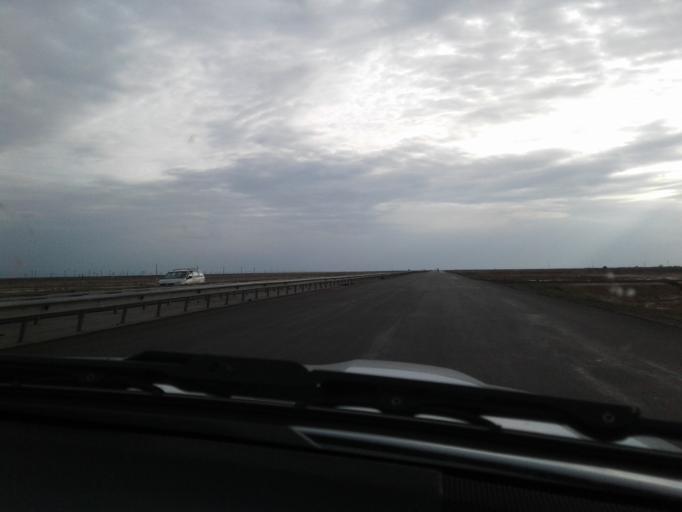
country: TM
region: Ahal
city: Tejen
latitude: 37.3516
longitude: 60.4175
